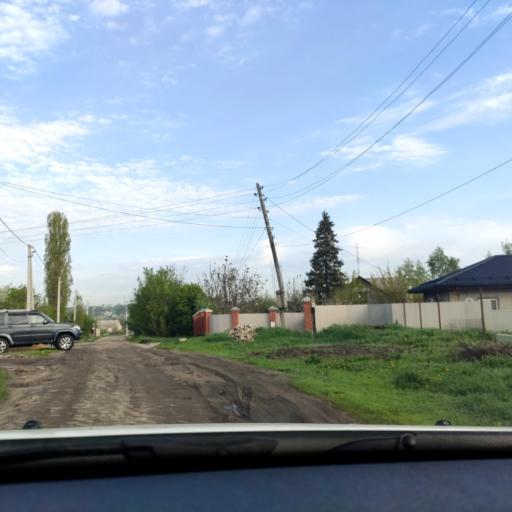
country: RU
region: Voronezj
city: Devitsa
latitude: 51.6407
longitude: 38.9571
